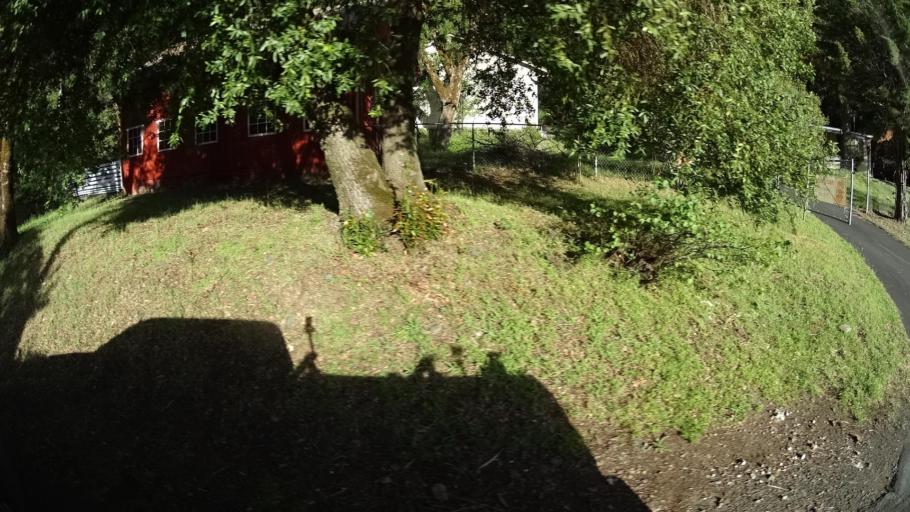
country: US
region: California
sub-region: Lake County
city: Upper Lake
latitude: 39.1532
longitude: -122.9987
